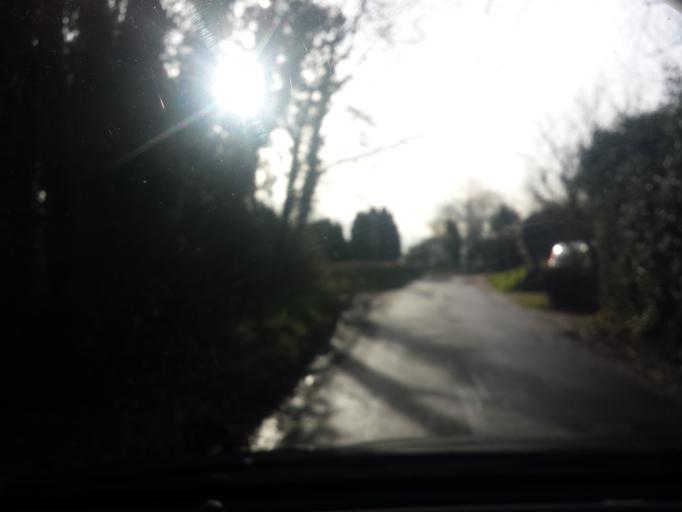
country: GB
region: England
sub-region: Essex
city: Alresford
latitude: 51.8964
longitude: 1.0278
